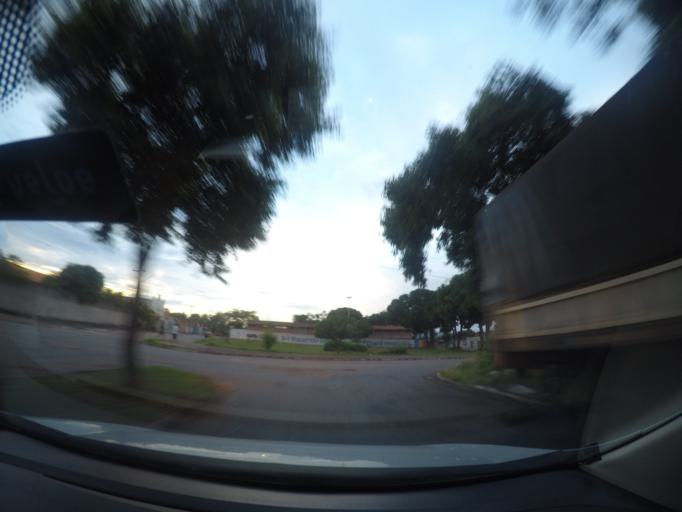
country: BR
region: Goias
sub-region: Goiania
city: Goiania
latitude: -16.7196
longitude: -49.3739
